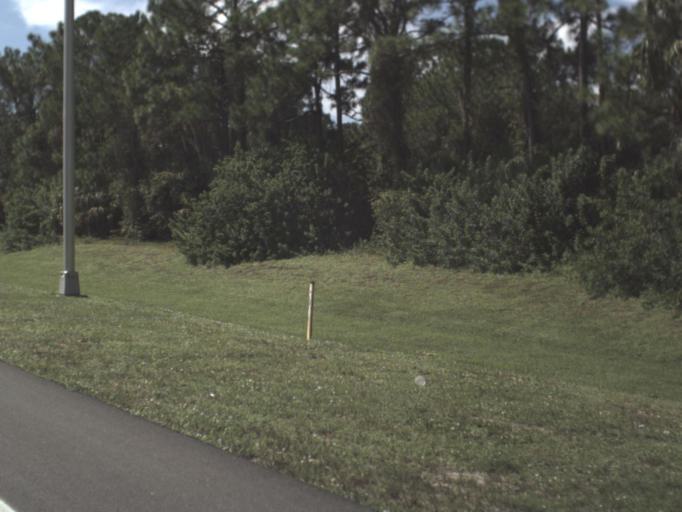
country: US
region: Florida
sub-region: Sarasota County
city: North Port
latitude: 27.0287
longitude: -82.1638
